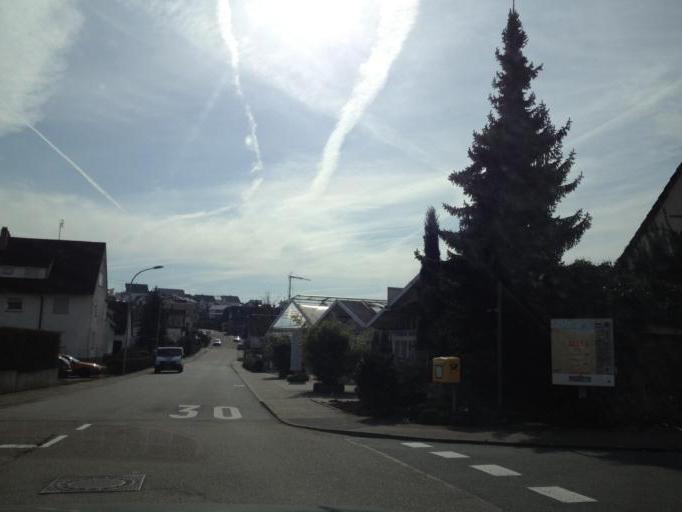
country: DE
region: Baden-Wuerttemberg
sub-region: Regierungsbezirk Stuttgart
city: Oedheim
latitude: 49.2427
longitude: 9.2627
